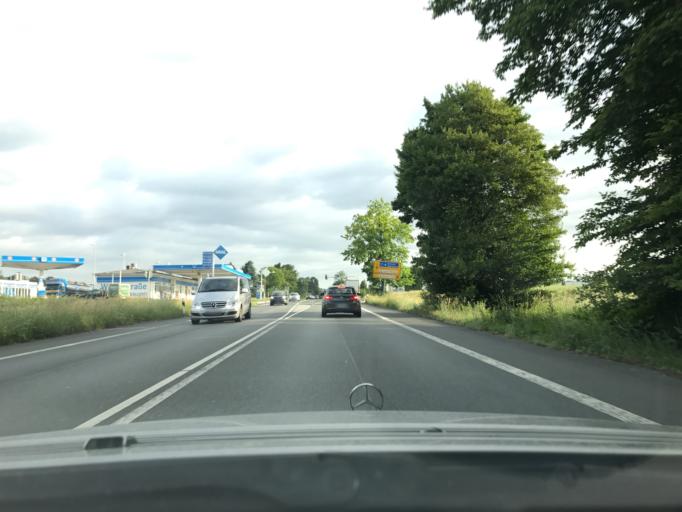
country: DE
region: North Rhine-Westphalia
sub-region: Regierungsbezirk Arnsberg
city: Hamm
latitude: 51.6159
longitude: 7.8498
